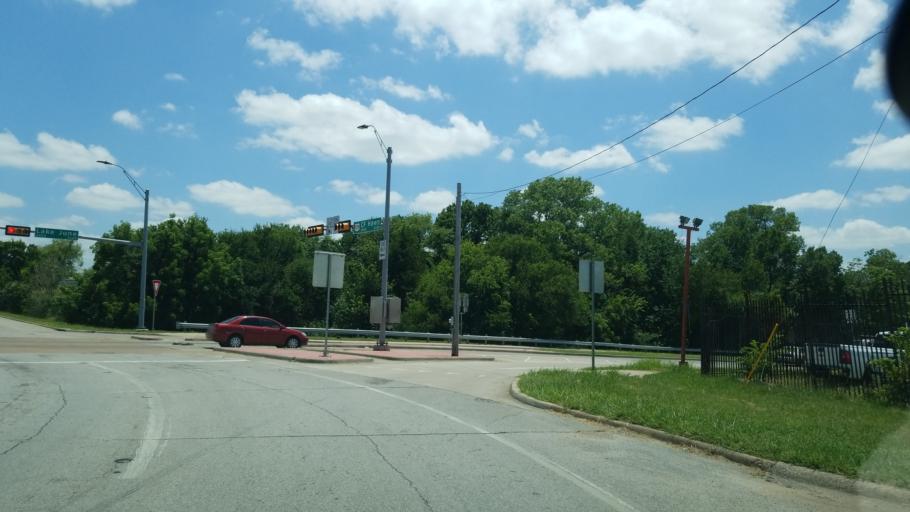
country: US
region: Texas
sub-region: Dallas County
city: Hutchins
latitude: 32.7334
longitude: -96.7145
